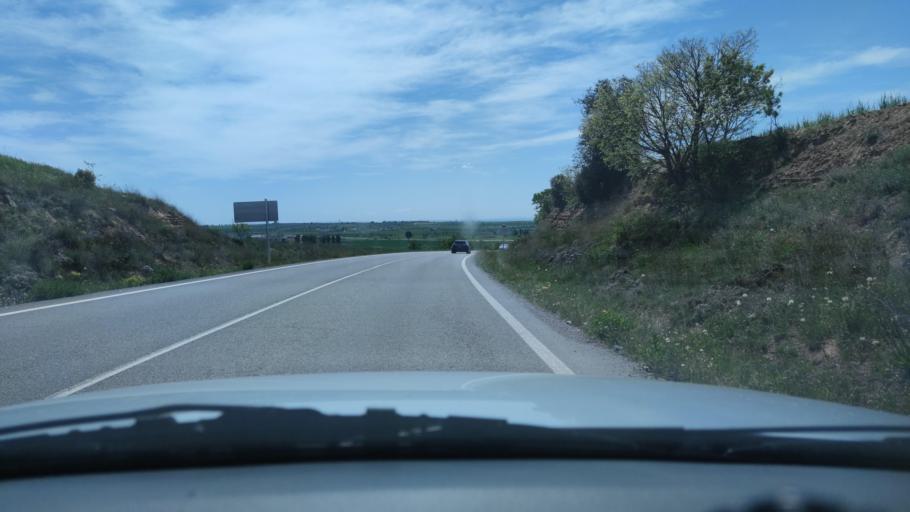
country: ES
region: Catalonia
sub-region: Provincia de Lleida
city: Mont-roig del Camp
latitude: 41.7935
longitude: 1.2781
